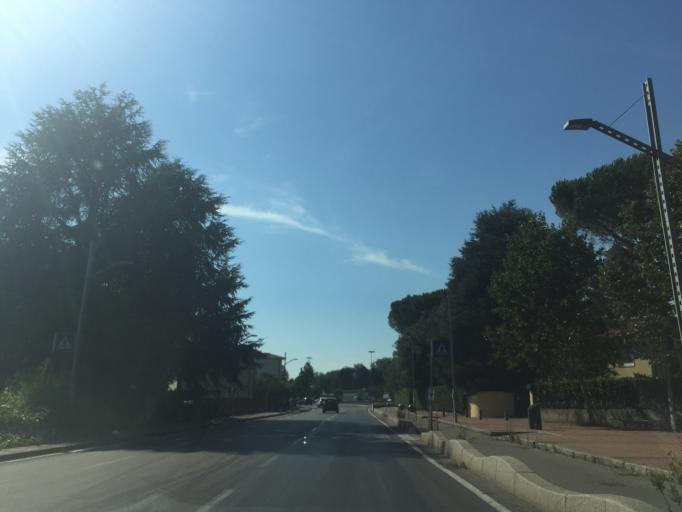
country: IT
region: Tuscany
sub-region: Provincia di Lucca
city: Lucca
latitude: 43.8498
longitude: 10.5037
